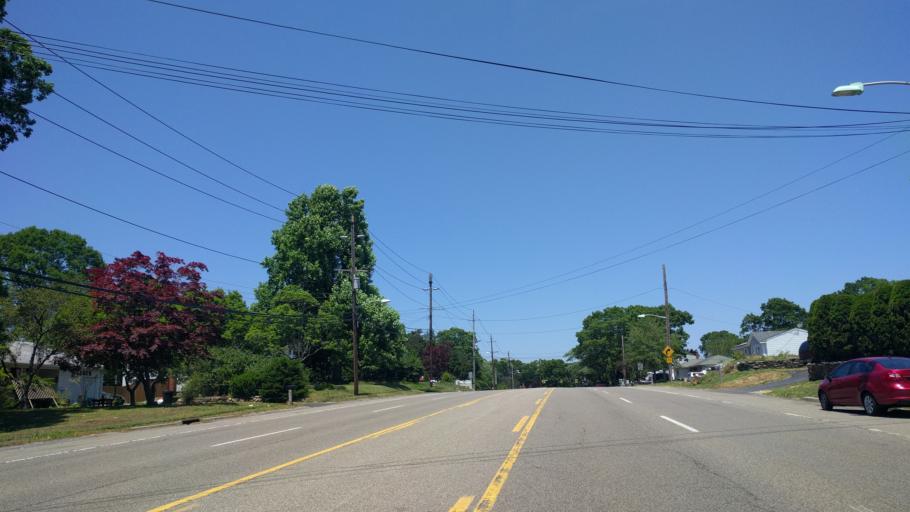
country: US
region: New York
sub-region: Suffolk County
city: Ronkonkoma
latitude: 40.8158
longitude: -73.1255
